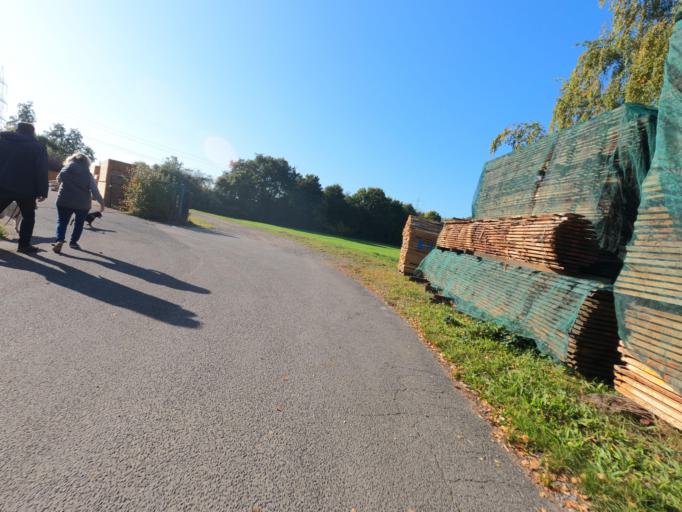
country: DE
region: North Rhine-Westphalia
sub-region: Regierungsbezirk Koln
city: Linnich
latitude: 50.9428
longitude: 6.2520
